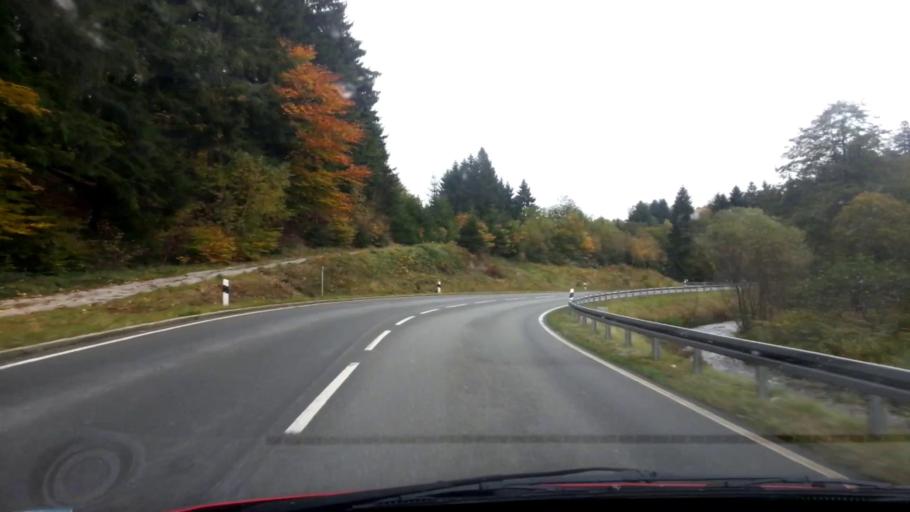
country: DE
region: Bavaria
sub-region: Upper Franconia
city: Warmensteinach
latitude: 49.9794
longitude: 11.7675
